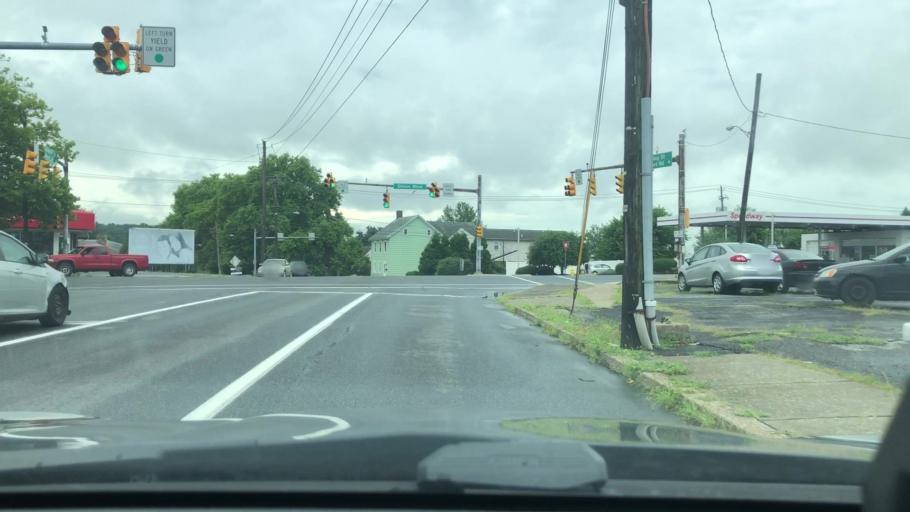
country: US
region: Pennsylvania
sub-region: Lehigh County
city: Fullerton
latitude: 40.6245
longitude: -75.4433
